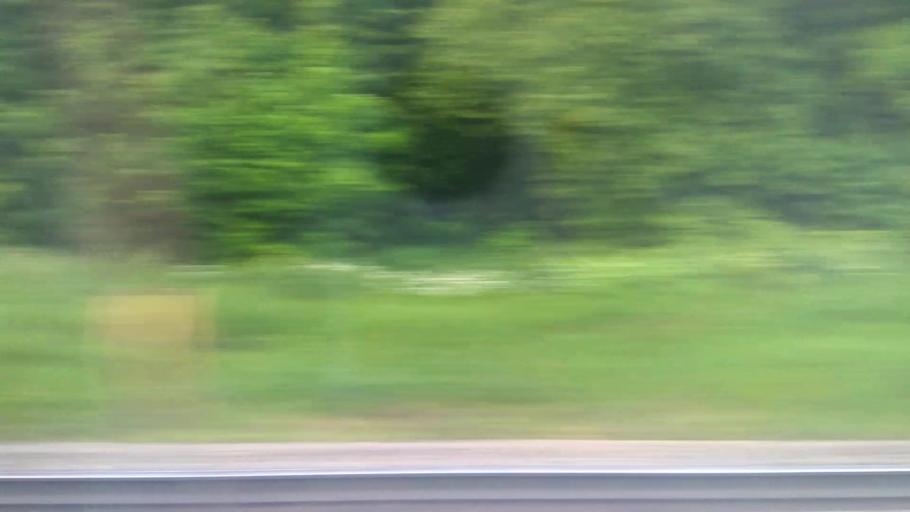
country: RU
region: Moskovskaya
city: Il'inskoye
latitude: 55.2078
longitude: 37.9195
